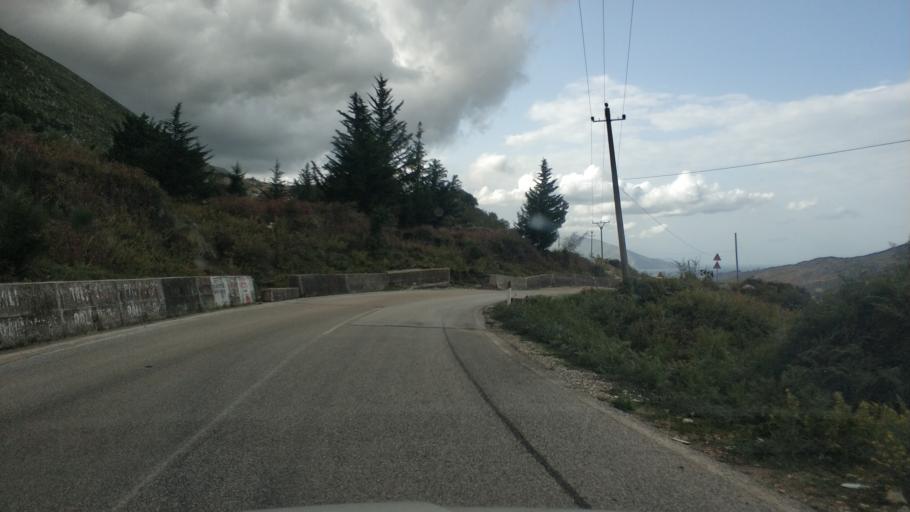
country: AL
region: Vlore
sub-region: Rrethi i Vlores
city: Orikum
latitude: 40.2615
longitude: 19.5235
